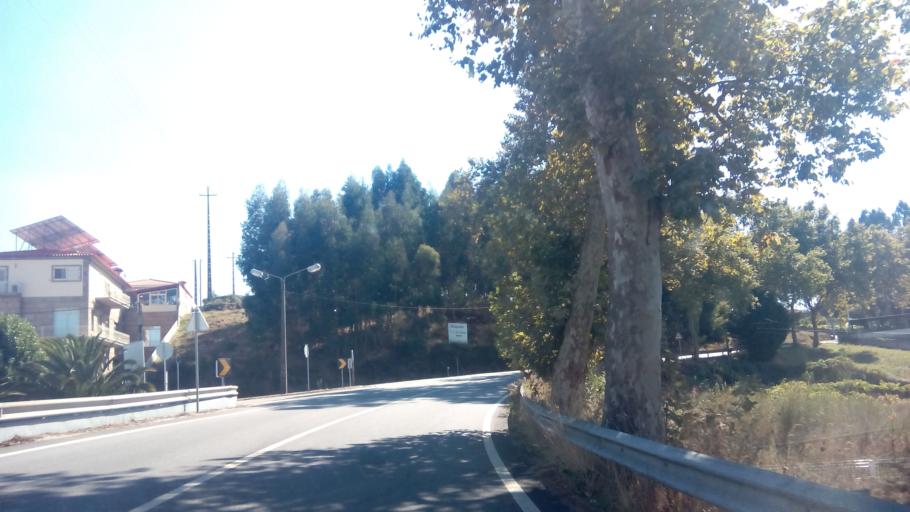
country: PT
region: Porto
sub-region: Lousada
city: Meinedo
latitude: 41.2442
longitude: -8.2148
